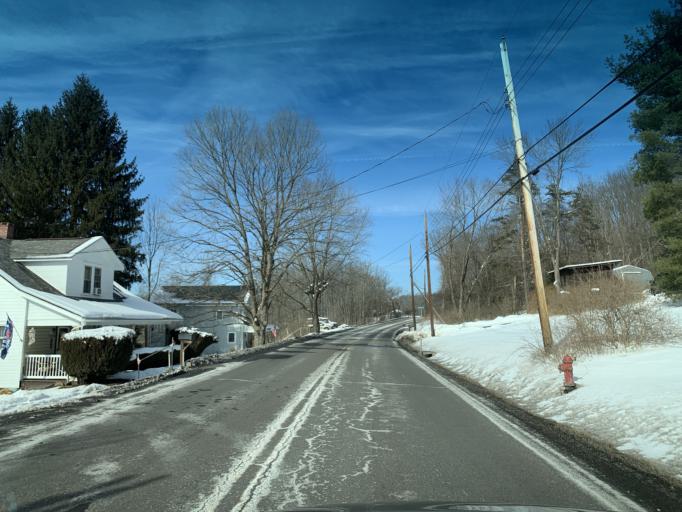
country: US
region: Maryland
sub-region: Allegany County
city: Frostburg
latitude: 39.6124
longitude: -78.9396
